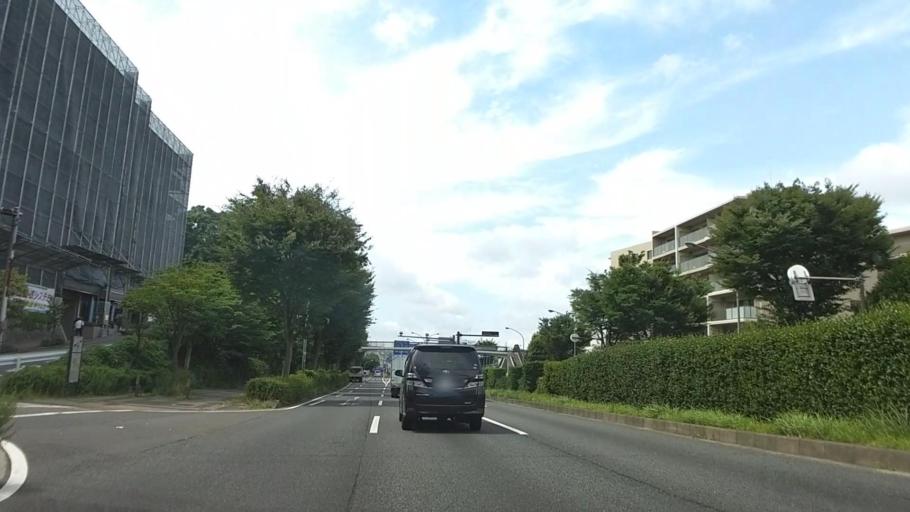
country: JP
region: Kanagawa
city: Yokohama
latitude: 35.4288
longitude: 139.5622
